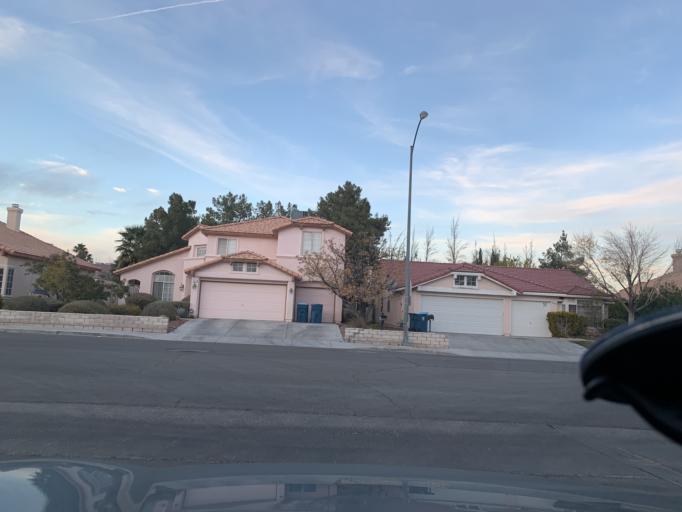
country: US
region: Nevada
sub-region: Clark County
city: Spring Valley
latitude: 36.0905
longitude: -115.2354
